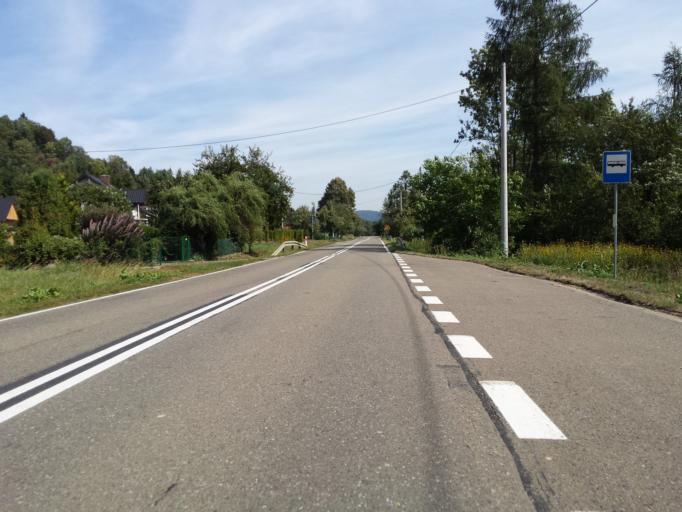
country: PL
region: Subcarpathian Voivodeship
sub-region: Powiat leski
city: Lesko
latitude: 49.4091
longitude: 22.2998
